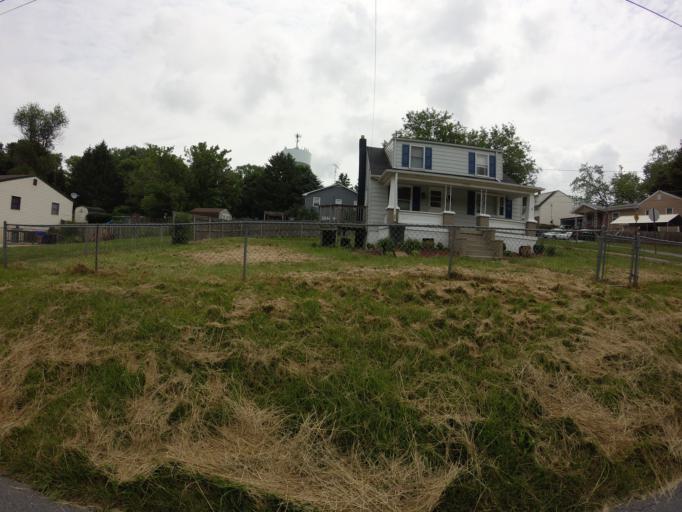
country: US
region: Maryland
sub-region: Frederick County
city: Brunswick
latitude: 39.3221
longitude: -77.6187
